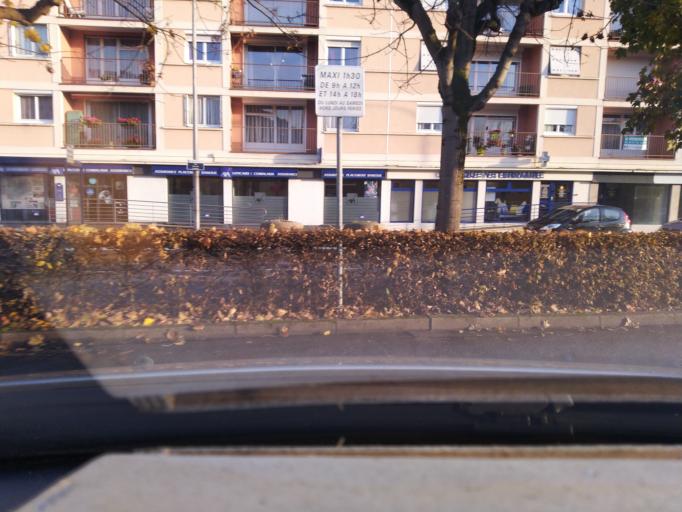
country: FR
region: Haute-Normandie
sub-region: Departement de la Seine-Maritime
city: Darnetal
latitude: 49.4400
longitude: 1.1455
